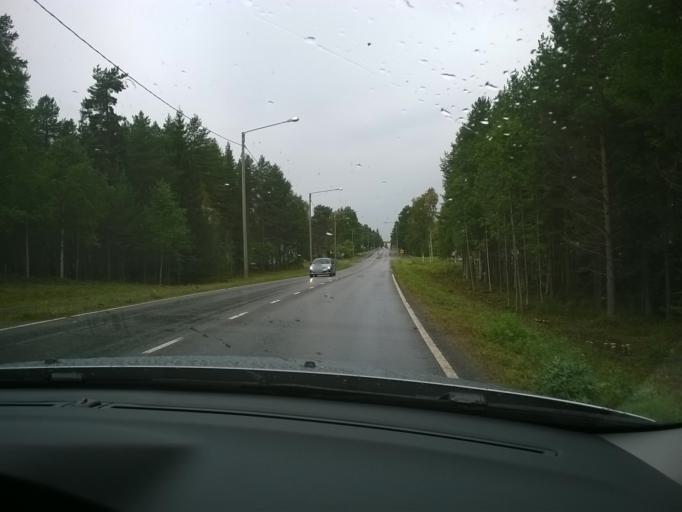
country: FI
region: Kainuu
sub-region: Kehys-Kainuu
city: Kuhmo
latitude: 64.1222
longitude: 29.5378
